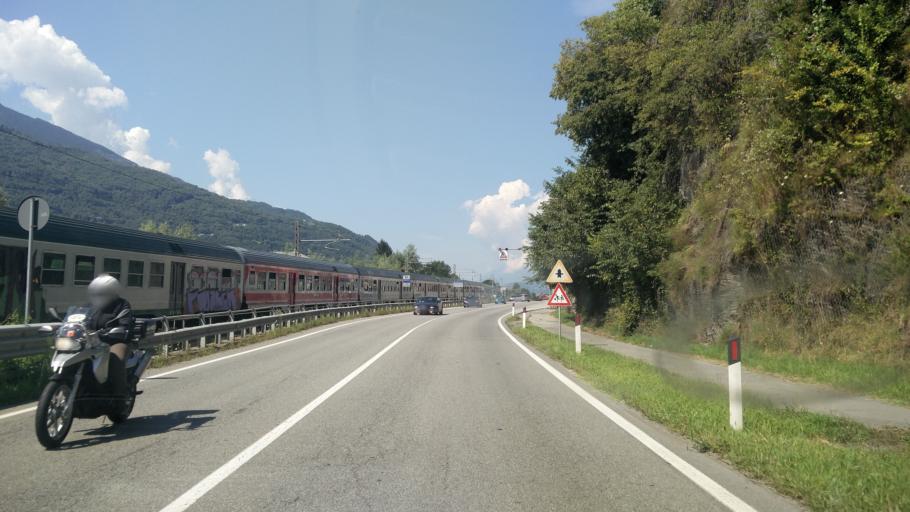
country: IT
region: Lombardy
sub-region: Provincia di Sondrio
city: San Giacomo
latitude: 46.1589
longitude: 10.0386
